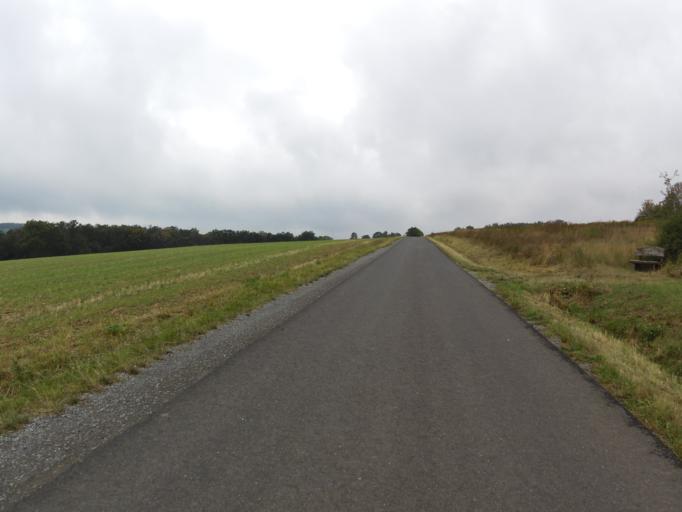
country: DE
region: Bavaria
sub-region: Regierungsbezirk Unterfranken
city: Guntersleben
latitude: 49.8583
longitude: 9.9123
